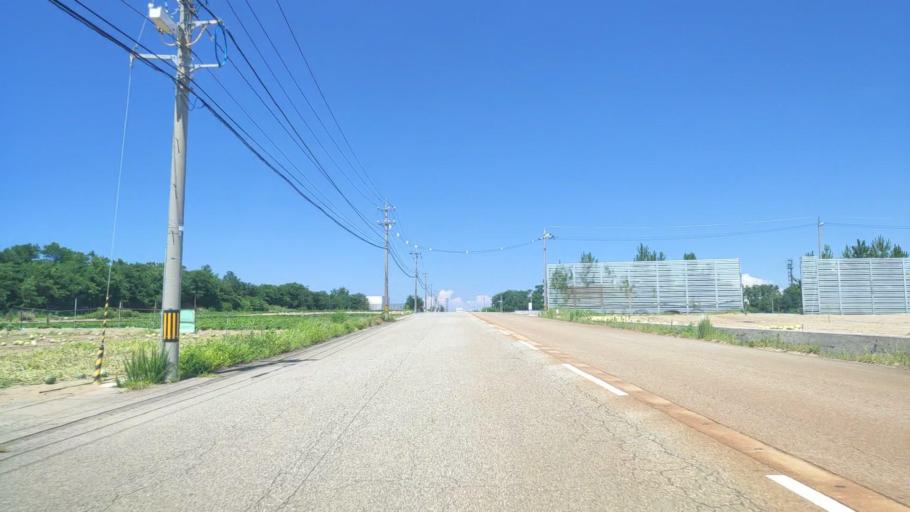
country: JP
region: Ishikawa
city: Kanazawa-shi
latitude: 36.6219
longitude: 136.6141
